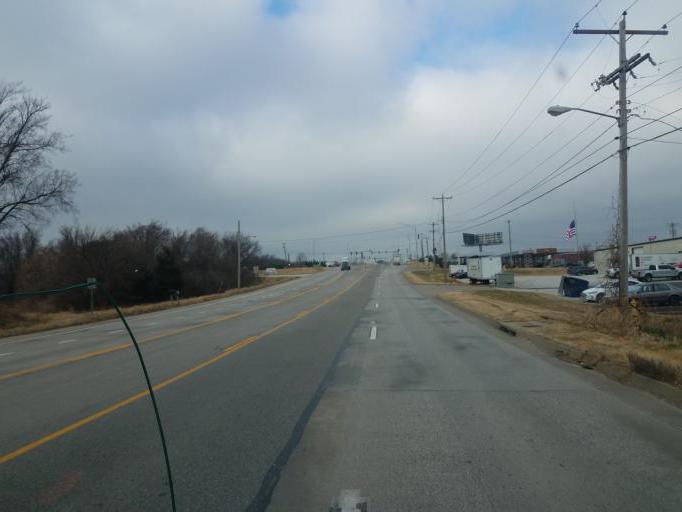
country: US
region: Missouri
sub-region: Greene County
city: Springfield
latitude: 37.2388
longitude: -93.2211
